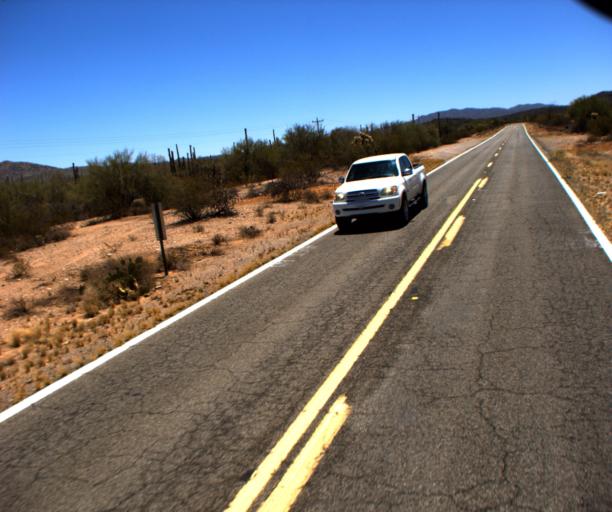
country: US
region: Arizona
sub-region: Pima County
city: Sells
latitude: 32.1804
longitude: -112.2778
